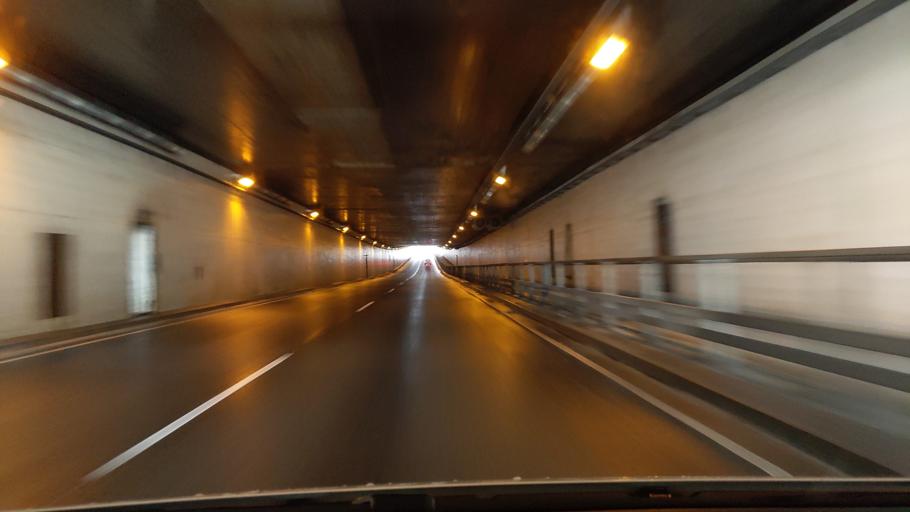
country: DK
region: Capital Region
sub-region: Tarnby Kommune
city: Tarnby
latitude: 55.6020
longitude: 12.6214
